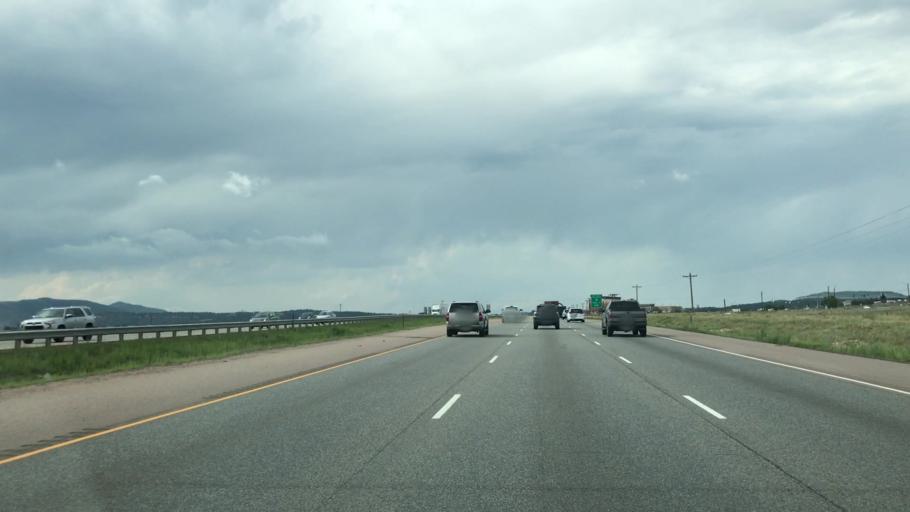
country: US
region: Colorado
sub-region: El Paso County
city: Monument
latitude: 39.0744
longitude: -104.8582
